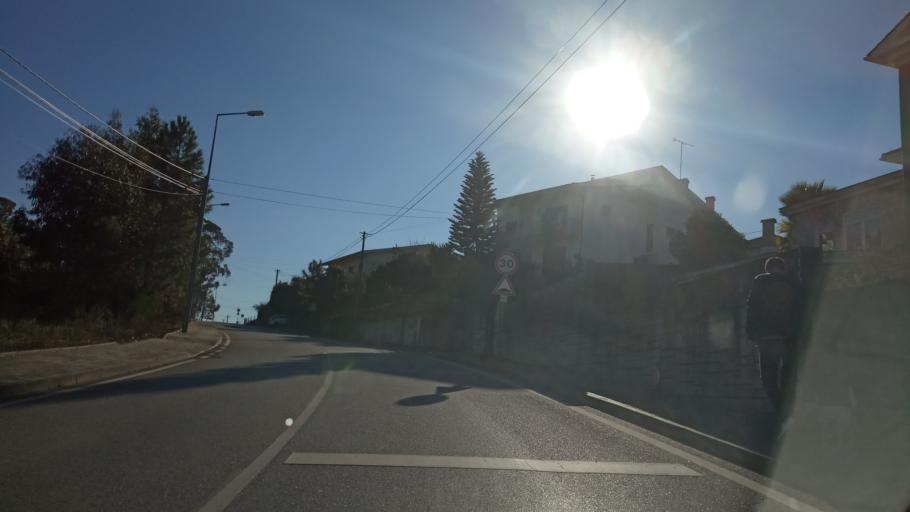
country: PT
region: Aveiro
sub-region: Anadia
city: Anadia
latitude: 40.4298
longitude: -8.4342
